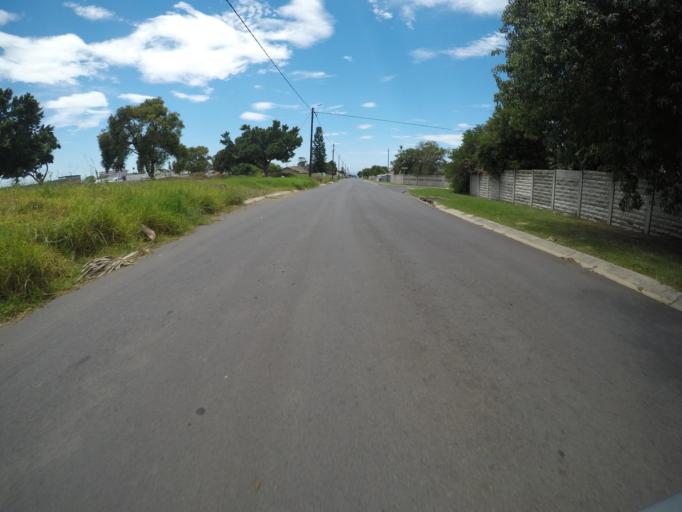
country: ZA
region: Eastern Cape
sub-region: Buffalo City Metropolitan Municipality
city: East London
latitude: -33.0363
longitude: 27.8529
